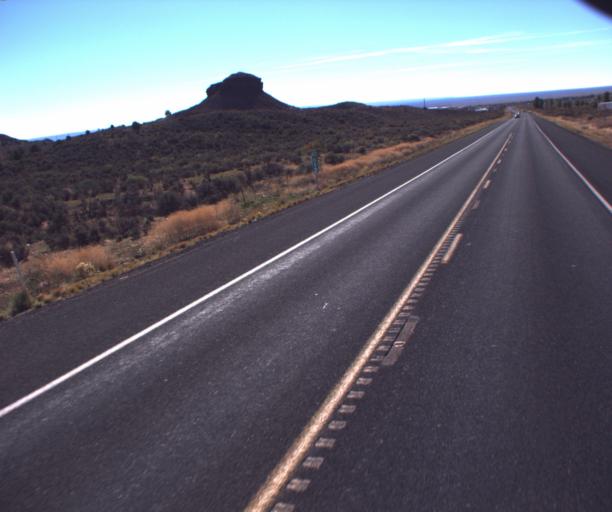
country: US
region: Arizona
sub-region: Coconino County
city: Fredonia
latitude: 36.9855
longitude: -112.5299
